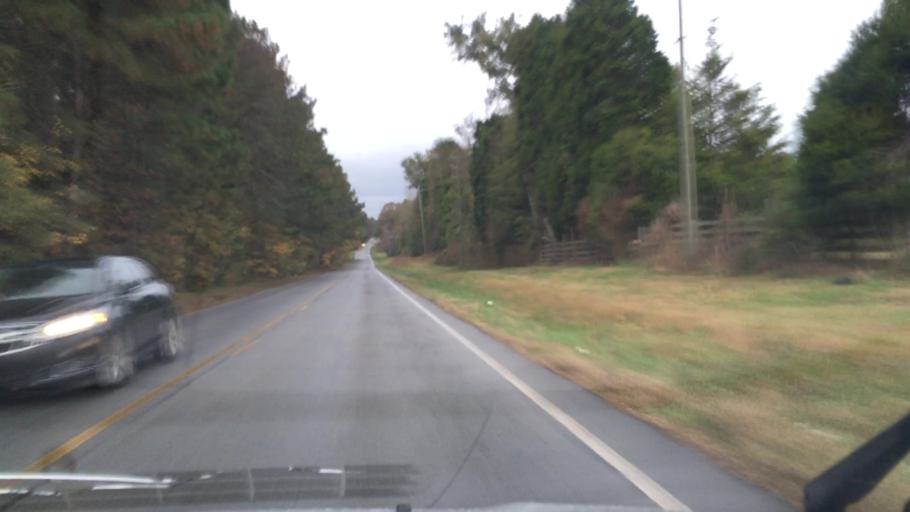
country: US
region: Georgia
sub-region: Henry County
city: Stockbridge
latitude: 33.5320
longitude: -84.1704
